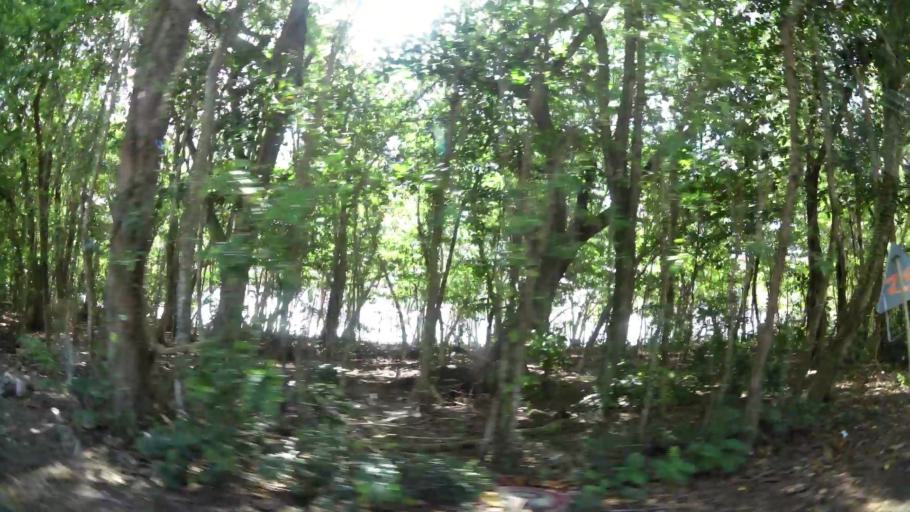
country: MQ
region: Martinique
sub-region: Martinique
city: Les Trois-Ilets
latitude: 14.4758
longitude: -61.0382
